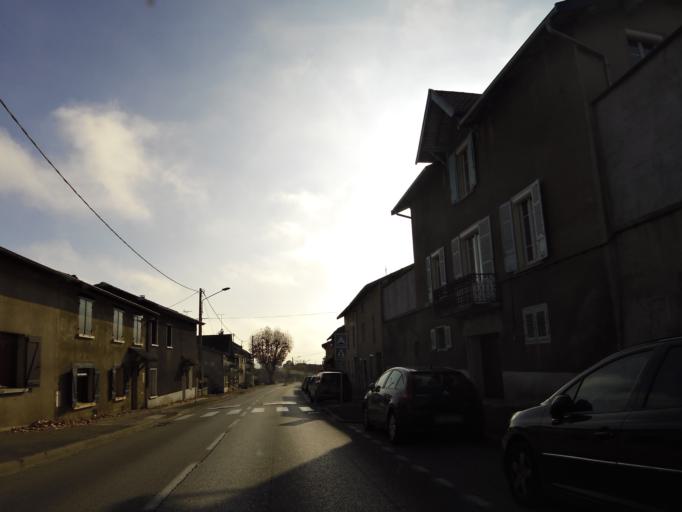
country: FR
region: Rhone-Alpes
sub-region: Departement de l'Ain
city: Meximieux
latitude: 45.9082
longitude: 5.1948
